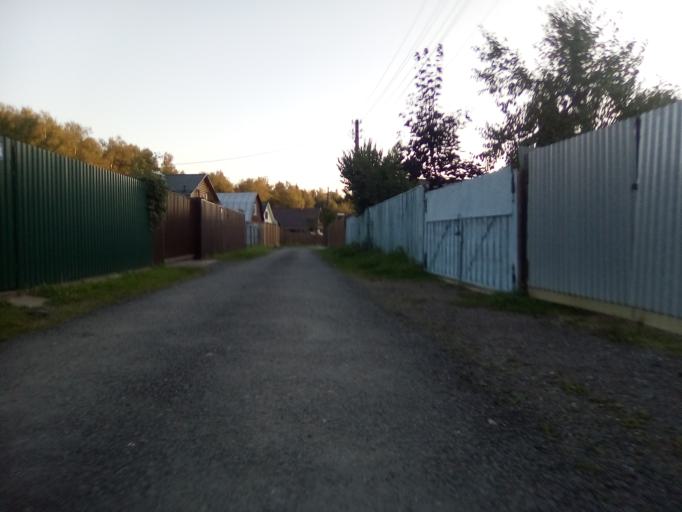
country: RU
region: Moskovskaya
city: Krasnoznamensk
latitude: 55.5620
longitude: 37.0283
